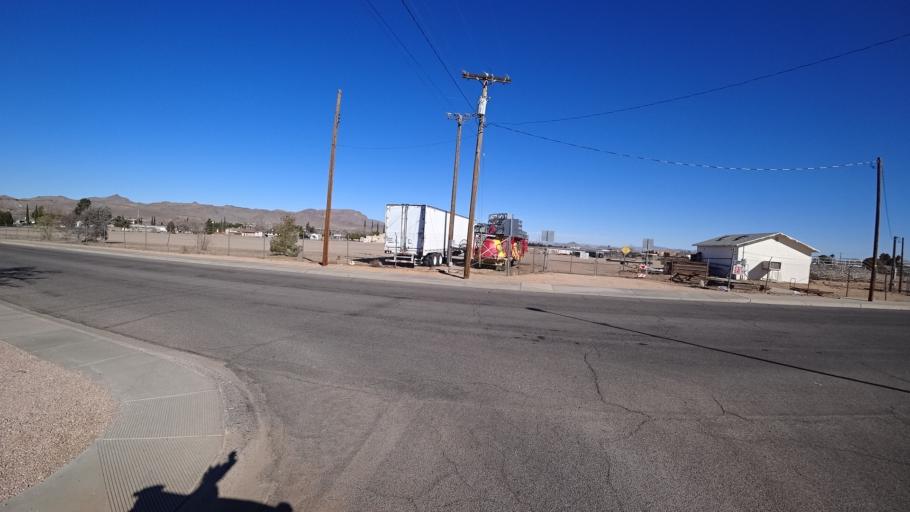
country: US
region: Arizona
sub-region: Mohave County
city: Kingman
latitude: 35.2088
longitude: -114.0270
